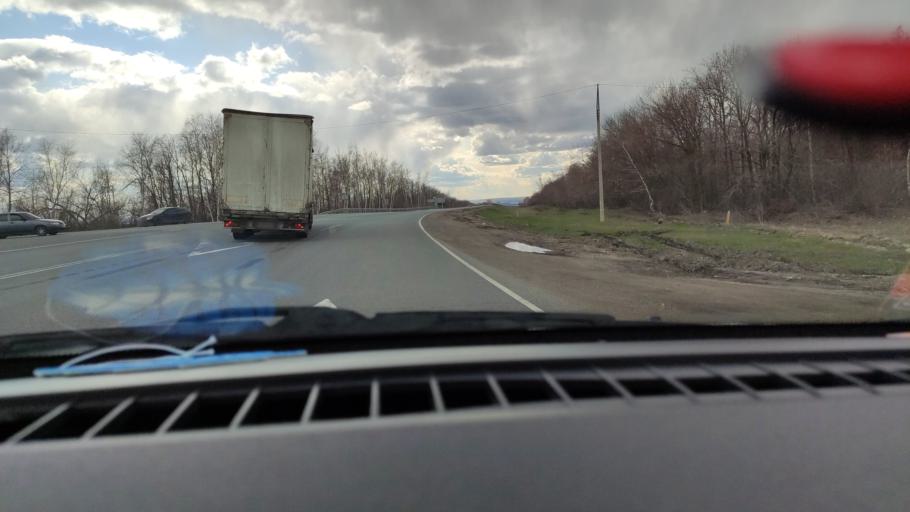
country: RU
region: Saratov
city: Balakovo
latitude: 52.0955
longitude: 47.7223
